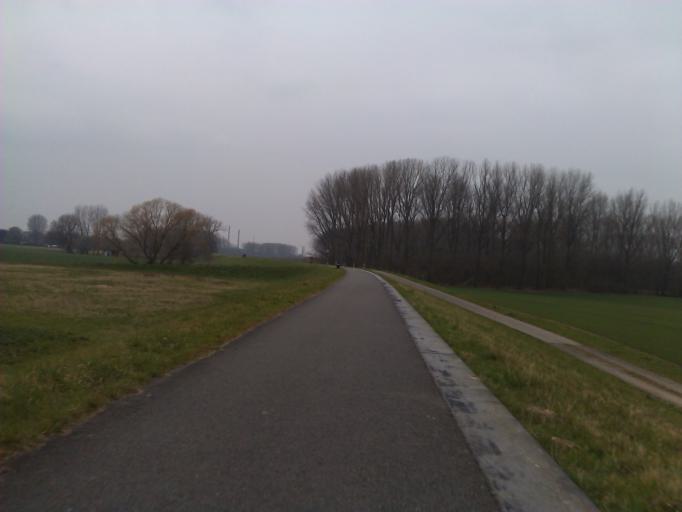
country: DE
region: North Rhine-Westphalia
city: Monheim am Rhein
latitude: 51.0620
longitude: 6.8898
